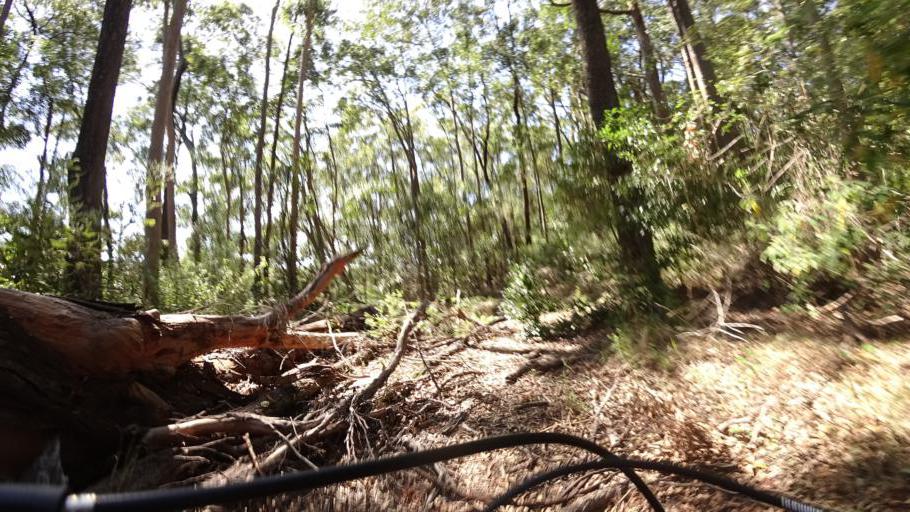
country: AU
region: Queensland
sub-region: Moreton Bay
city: Highvale
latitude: -27.4127
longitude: 152.7835
